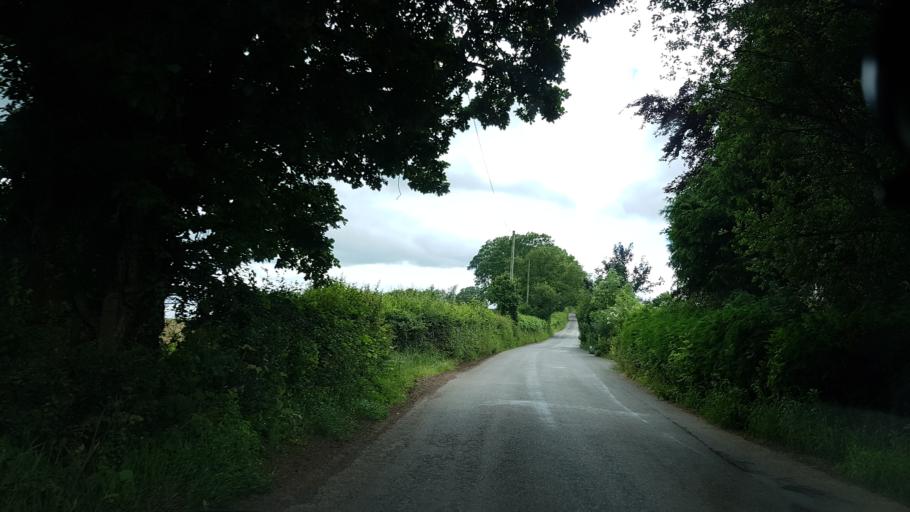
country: GB
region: England
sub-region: Herefordshire
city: Llancillo
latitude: 51.8877
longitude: -2.9498
